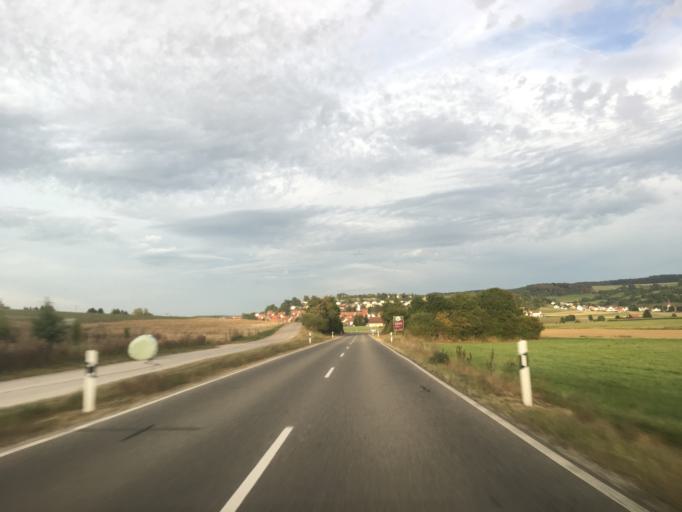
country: DE
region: Baden-Wuerttemberg
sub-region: Tuebingen Region
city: Sankt Johann
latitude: 48.4366
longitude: 9.3570
